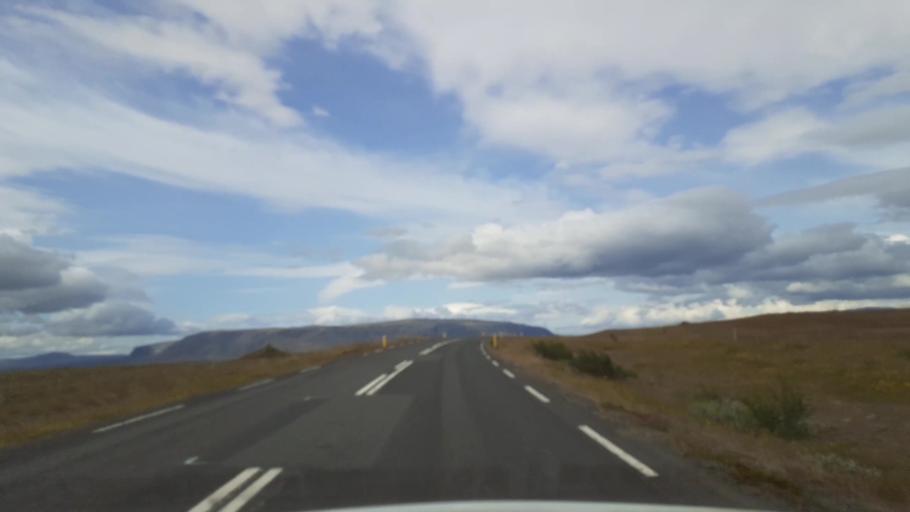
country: IS
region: South
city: Selfoss
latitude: 63.9196
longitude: -20.8480
